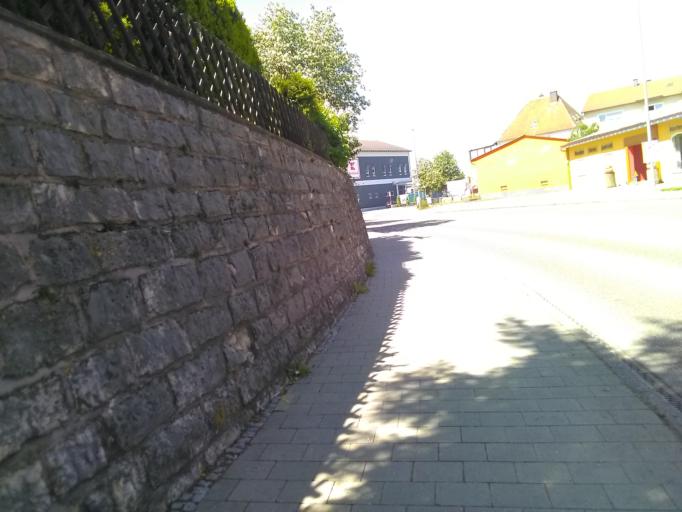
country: DE
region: Bavaria
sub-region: Regierungsbezirk Mittelfranken
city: Gunzenhausen
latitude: 49.1210
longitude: 10.7539
